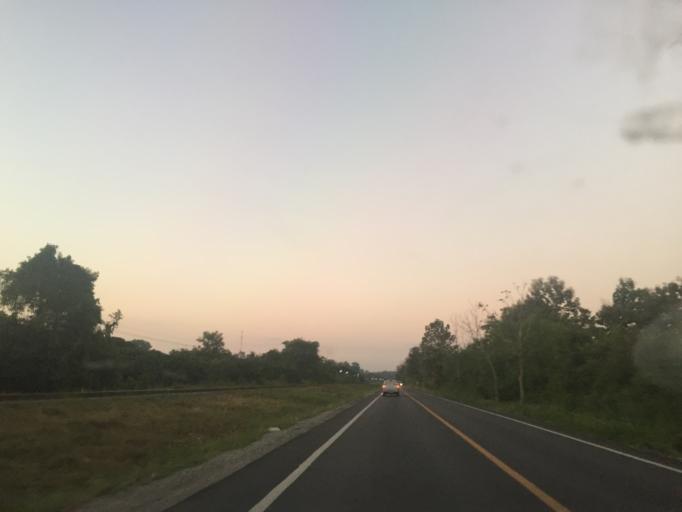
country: TH
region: Chiang Mai
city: Saraphi
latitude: 18.6699
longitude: 99.0446
